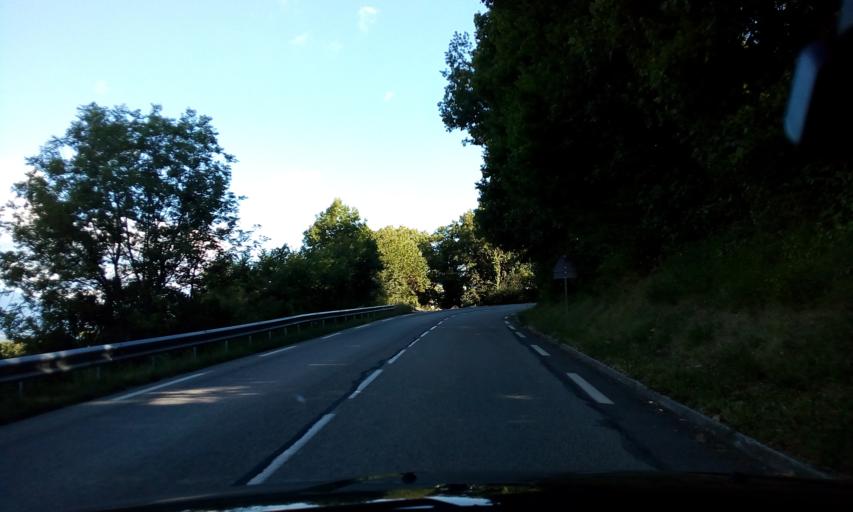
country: FR
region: Rhone-Alpes
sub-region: Departement de l'Isere
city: Seyssins
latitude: 45.1634
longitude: 5.6703
